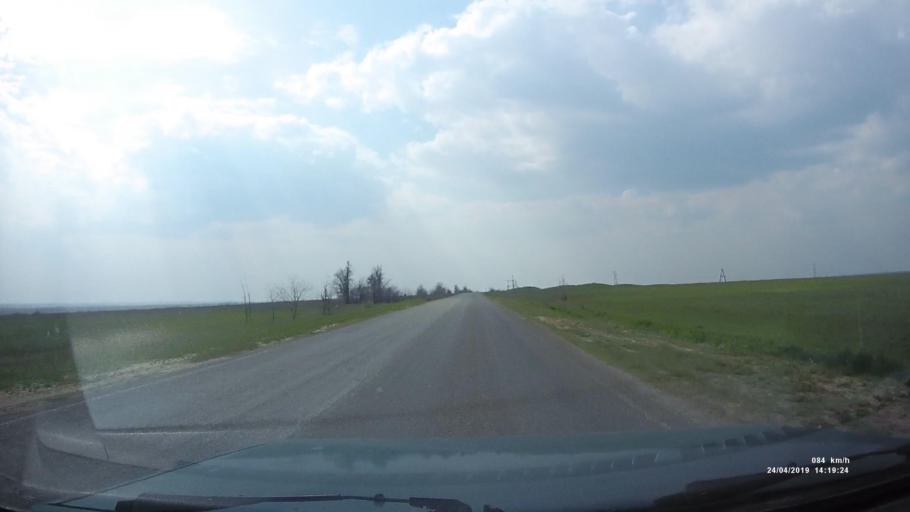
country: RU
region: Kalmykiya
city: Arshan'
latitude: 46.3053
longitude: 44.1763
